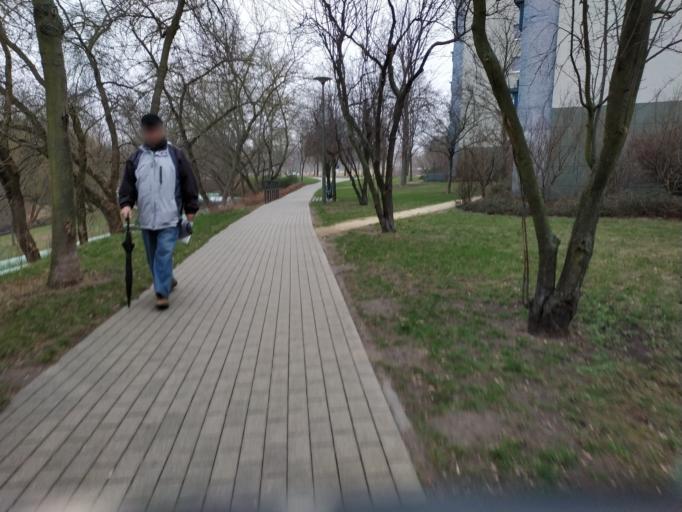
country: DE
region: Berlin
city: Marzahn
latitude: 52.5388
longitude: 13.5847
